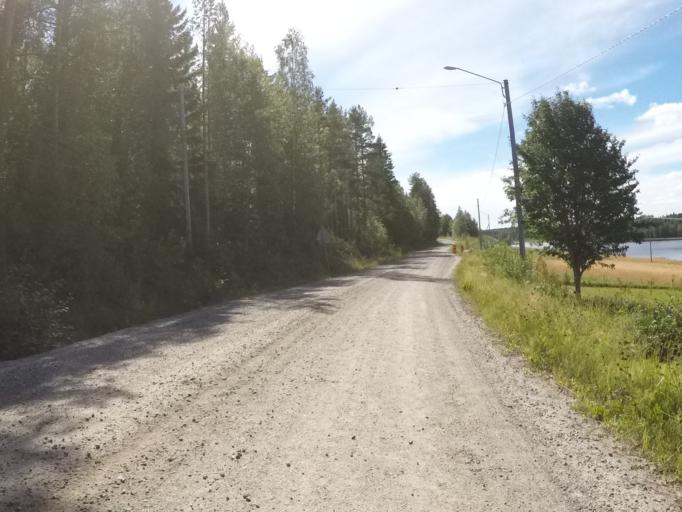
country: SE
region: Vaesterbotten
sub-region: Robertsfors Kommun
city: Robertsfors
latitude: 64.0083
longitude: 20.8168
